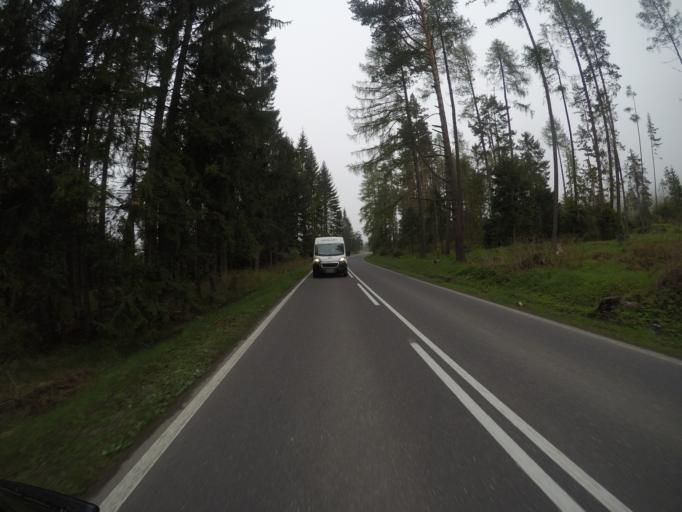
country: SK
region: Presovsky
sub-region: Okres Poprad
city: Strba
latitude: 49.0983
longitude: 20.0679
